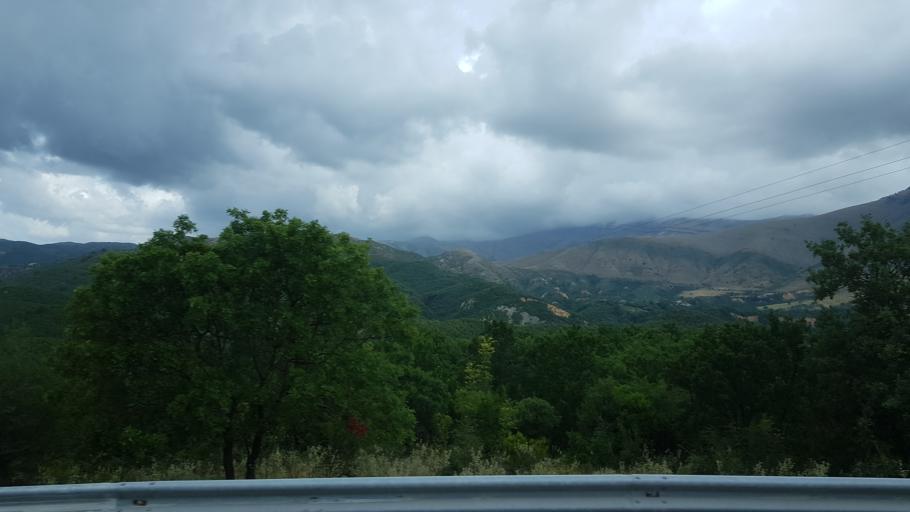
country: AL
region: Vlore
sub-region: Rrethi i Sarandes
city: Dhiver
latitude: 39.9168
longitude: 20.1918
